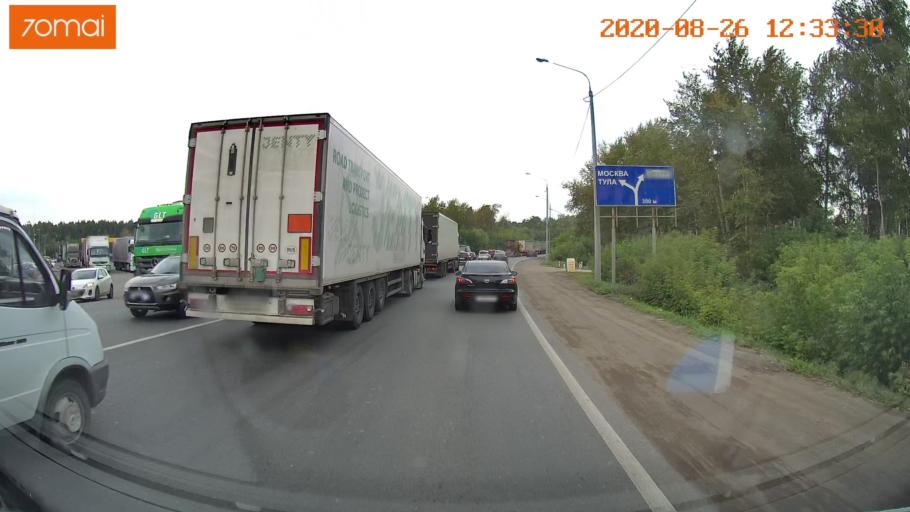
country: RU
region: Rjazan
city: Ryazan'
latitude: 54.5821
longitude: 39.7760
